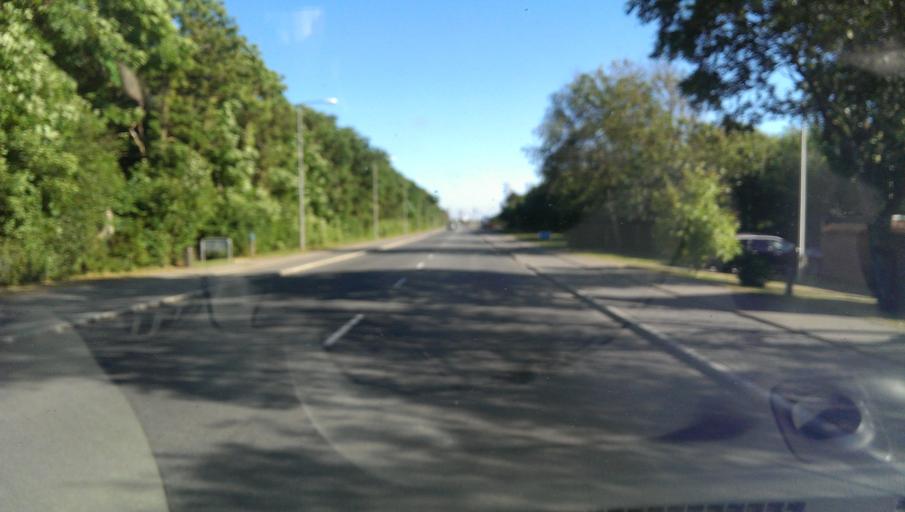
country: DK
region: South Denmark
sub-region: Esbjerg Kommune
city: Esbjerg
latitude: 55.4924
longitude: 8.4107
